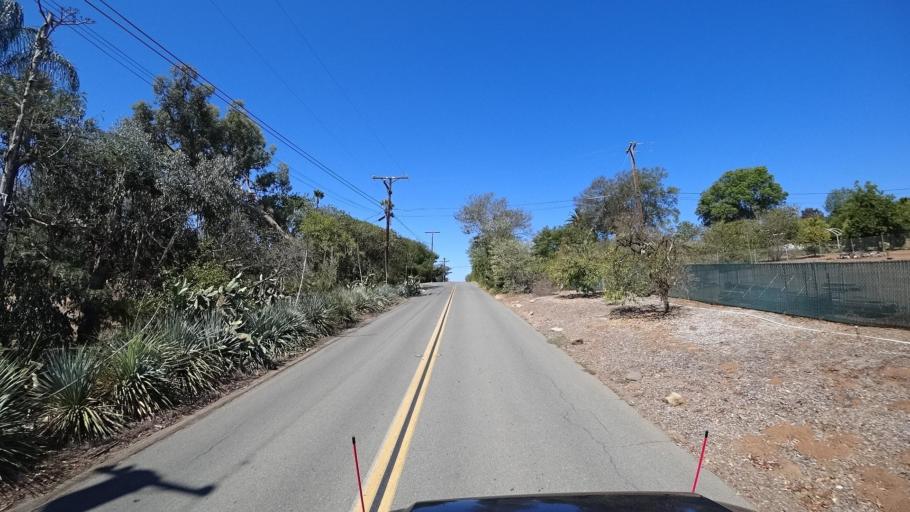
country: US
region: California
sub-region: San Diego County
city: Fallbrook
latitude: 33.3625
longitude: -117.2177
